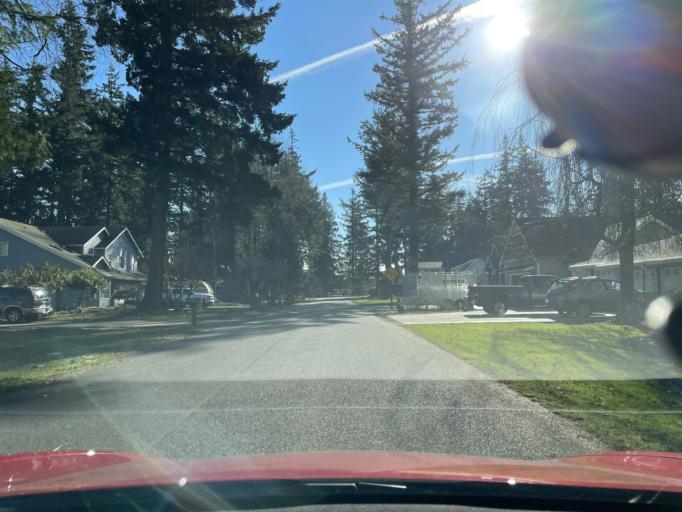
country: US
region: Washington
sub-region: Whatcom County
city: Lynden
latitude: 48.9536
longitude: -122.5080
